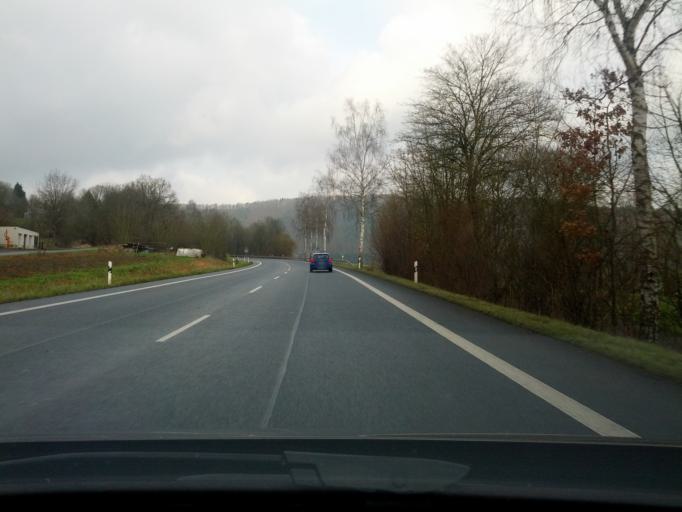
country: DE
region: Lower Saxony
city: Bodenfelde
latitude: 51.5870
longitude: 9.5830
